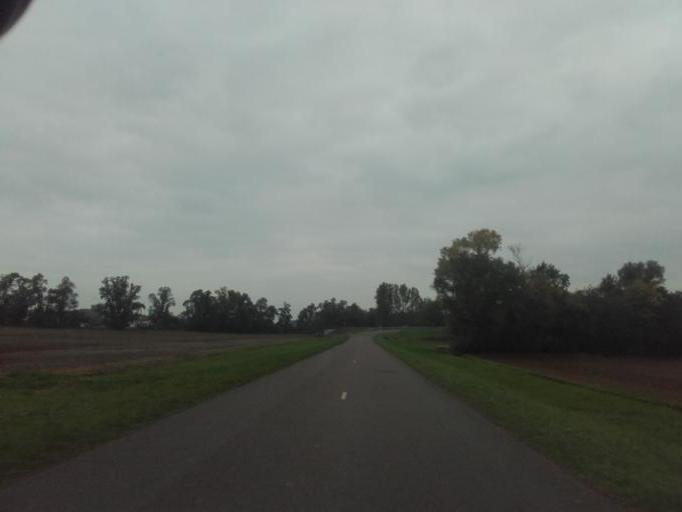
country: FR
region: Bourgogne
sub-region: Departement de Saone-et-Loire
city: Demigny
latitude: 46.9414
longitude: 4.8281
